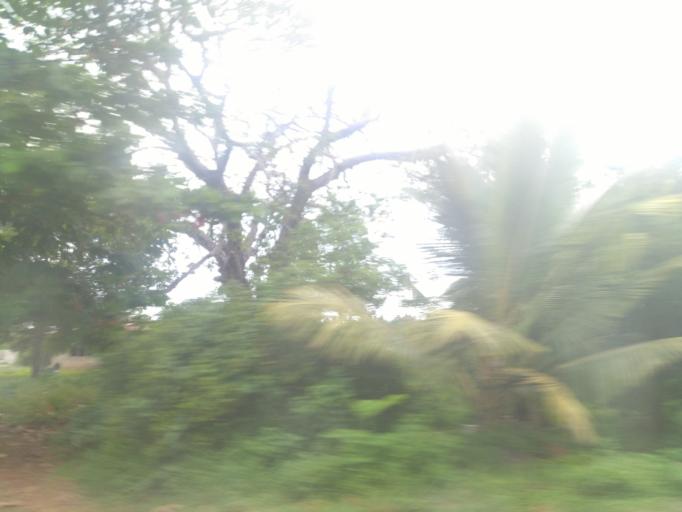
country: TZ
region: Zanzibar Urban/West
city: Zanzibar
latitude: -6.2660
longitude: 39.2638
